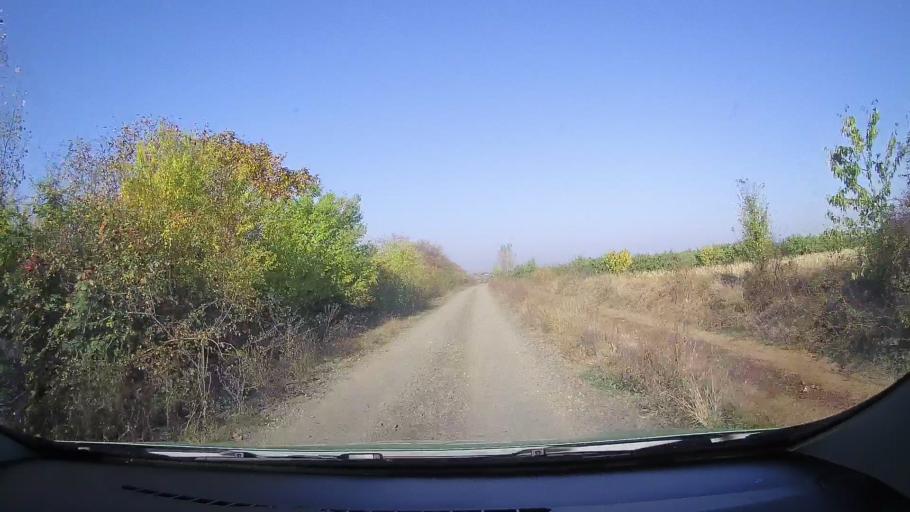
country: RO
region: Satu Mare
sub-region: Comuna Sauca
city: Sauca
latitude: 47.4762
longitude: 22.4770
